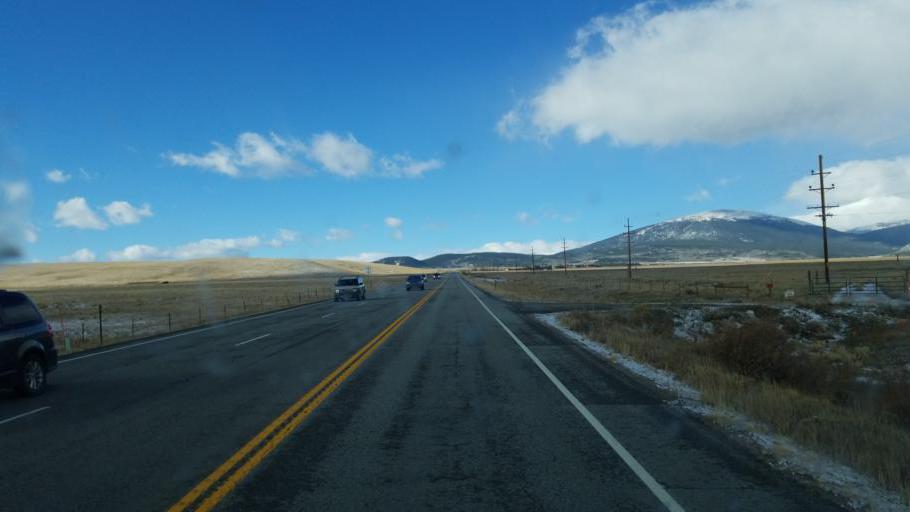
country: US
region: Colorado
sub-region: Park County
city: Fairplay
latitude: 39.3434
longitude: -105.8467
